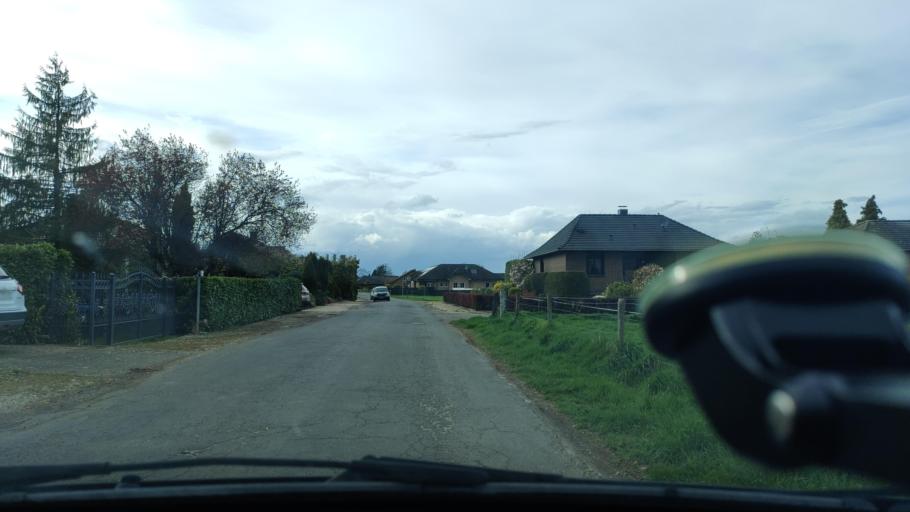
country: DE
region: North Rhine-Westphalia
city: Rees
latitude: 51.7407
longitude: 6.4016
